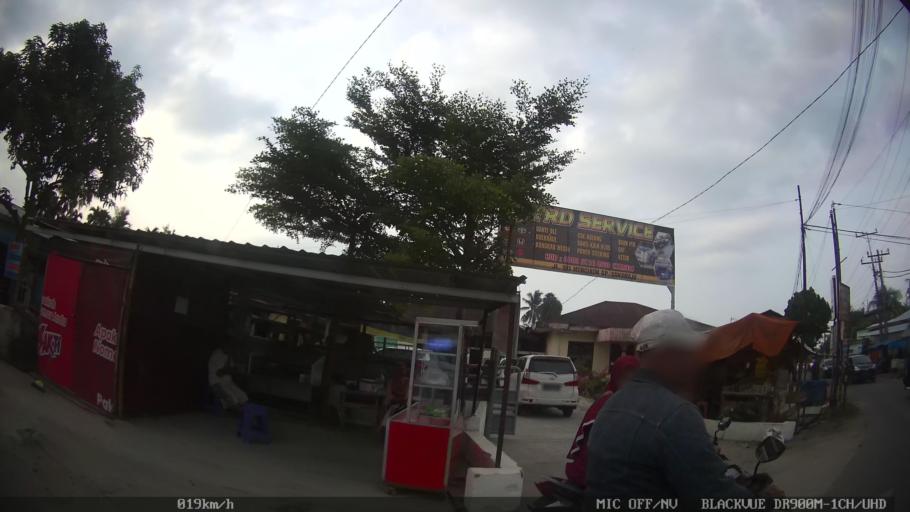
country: ID
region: North Sumatra
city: Sunggal
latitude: 3.5609
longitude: 98.5742
